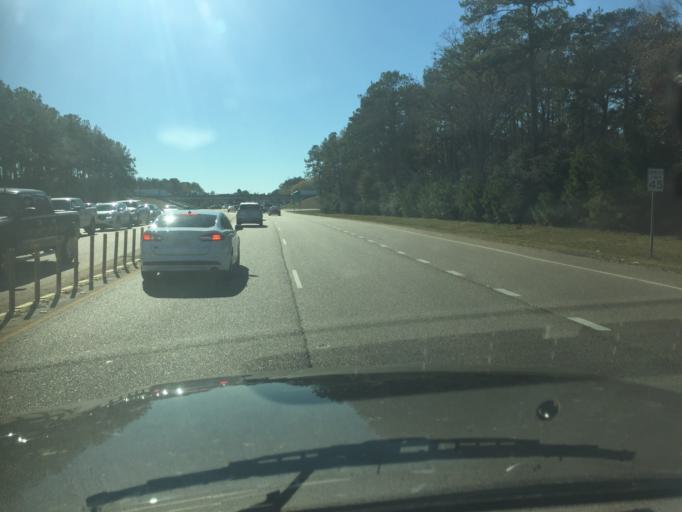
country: US
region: Louisiana
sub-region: Saint Tammany Parish
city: Covington
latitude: 30.4495
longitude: -90.1385
